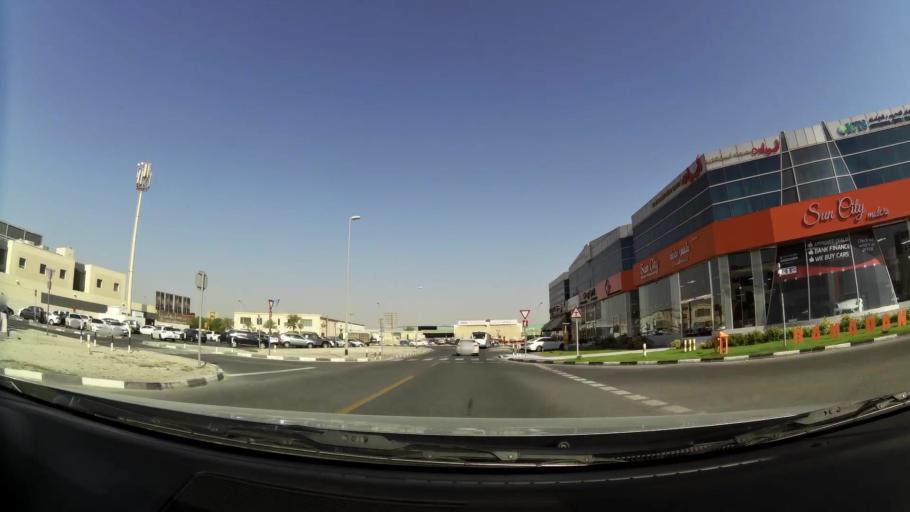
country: AE
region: Dubai
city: Dubai
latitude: 25.1247
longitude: 55.2079
